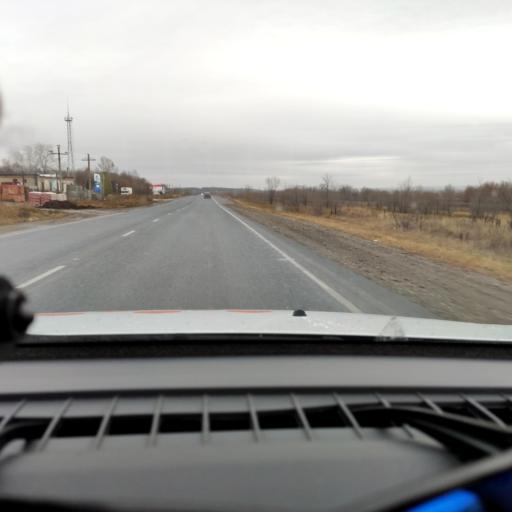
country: RU
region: Samara
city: Samara
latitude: 53.1248
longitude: 50.1818
